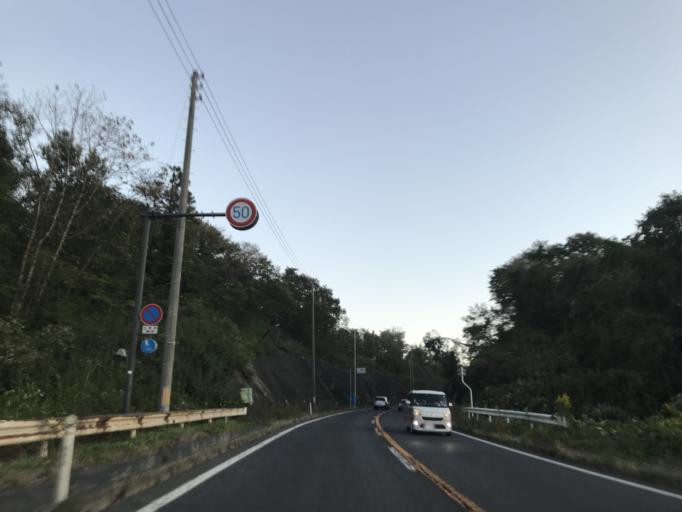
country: JP
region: Iwate
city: Ichinoseki
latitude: 38.9583
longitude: 141.1226
